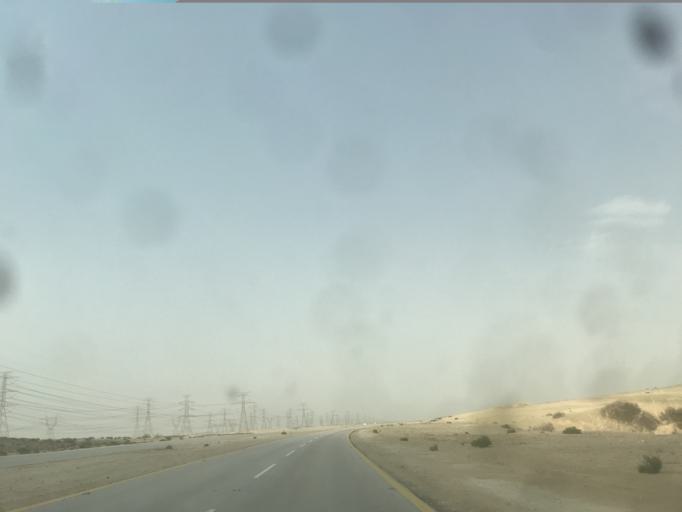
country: SA
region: Eastern Province
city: Abqaiq
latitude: 25.9075
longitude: 49.8946
